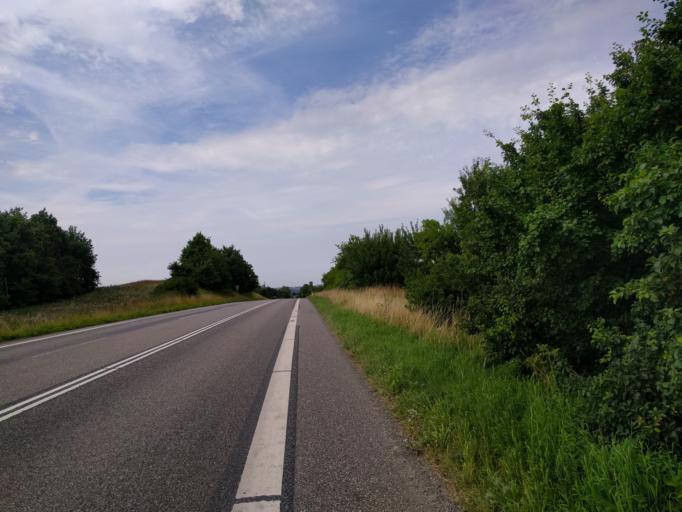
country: DK
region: Zealand
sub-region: Kalundborg Kommune
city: Svebolle
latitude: 55.6993
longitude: 11.3372
